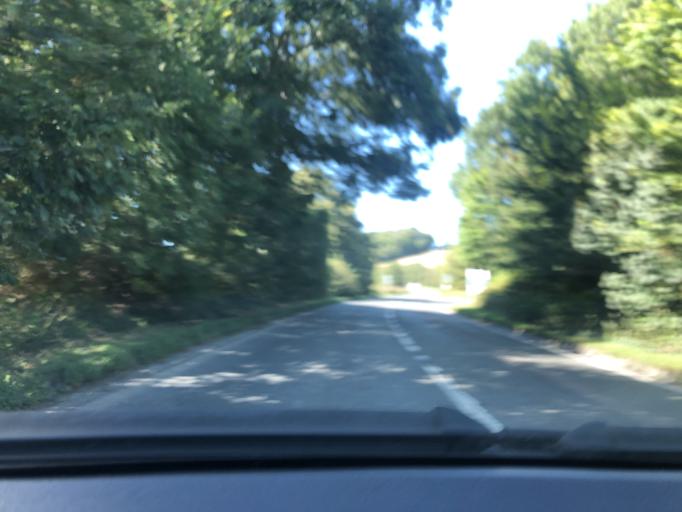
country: GB
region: England
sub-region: Somerset
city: Puriton
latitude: 51.1576
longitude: -2.9614
